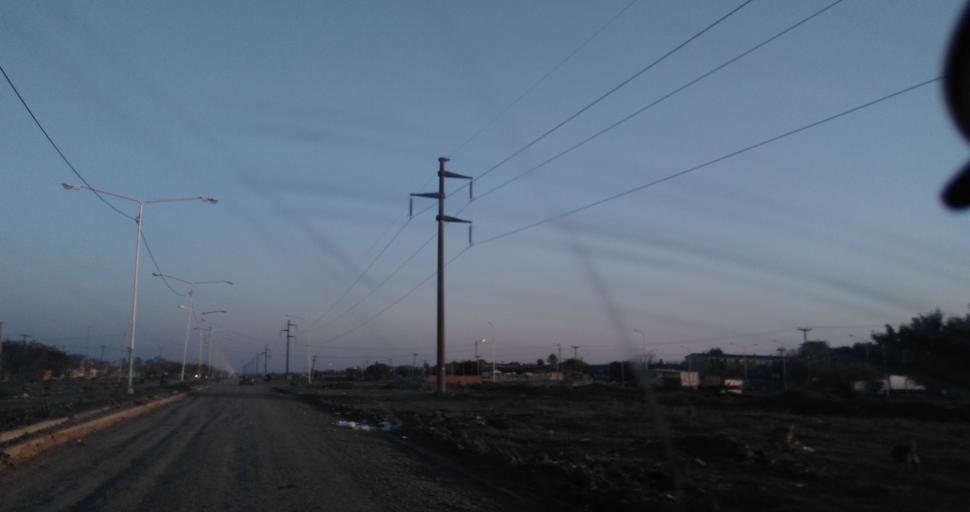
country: AR
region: Chaco
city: Resistencia
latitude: -27.4655
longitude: -59.0149
